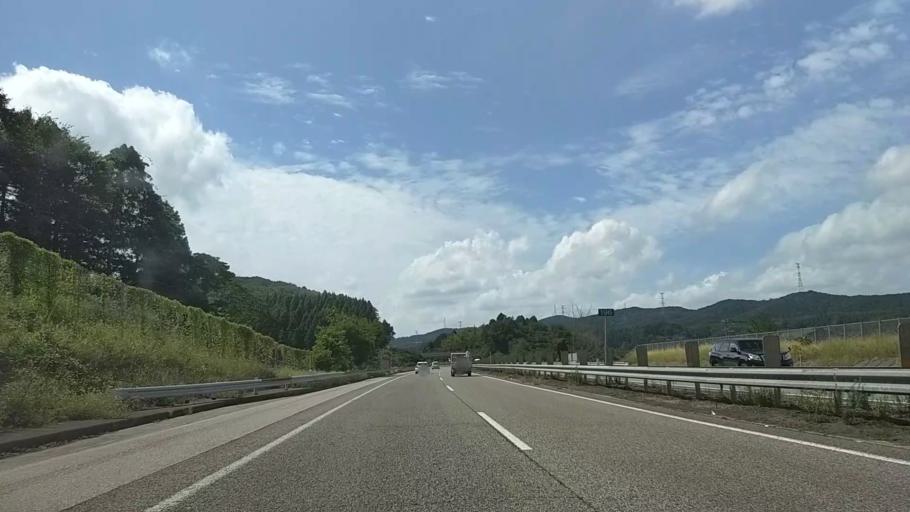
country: JP
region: Toyama
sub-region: Oyabe Shi
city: Oyabe
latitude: 36.6246
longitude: 136.8335
